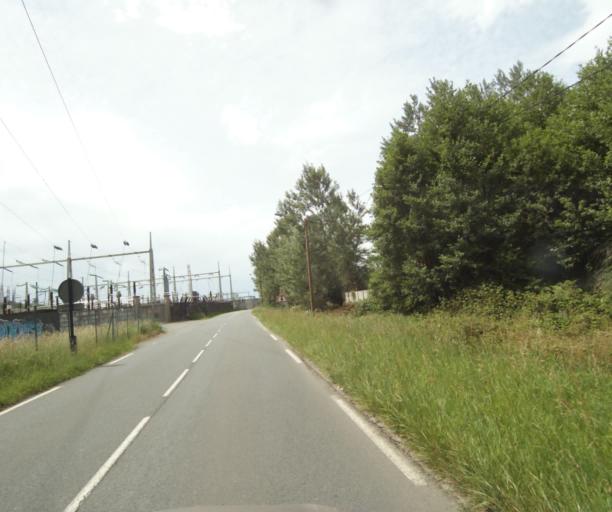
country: FR
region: Aquitaine
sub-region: Departement des Pyrenees-Atlantiques
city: Mouguerre
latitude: 43.4848
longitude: -1.4391
